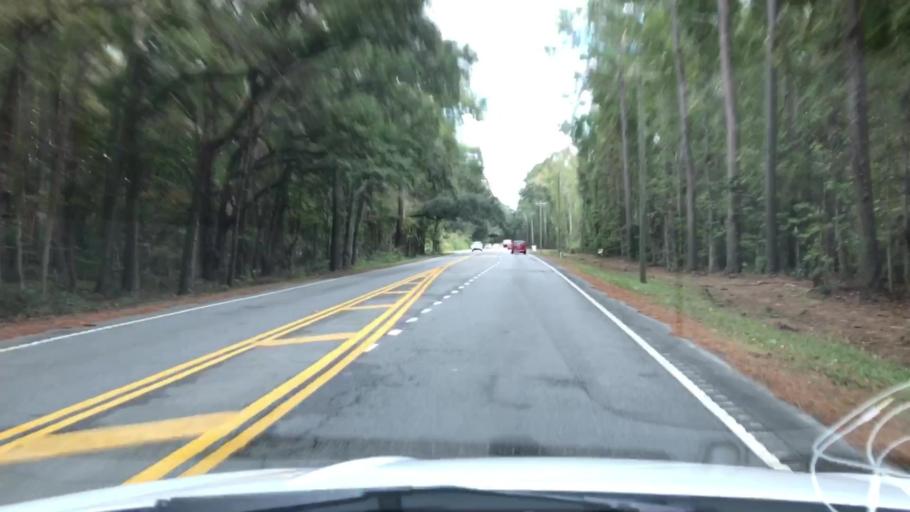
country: US
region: South Carolina
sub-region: Beaufort County
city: Bluffton
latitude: 32.2311
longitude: -80.9218
